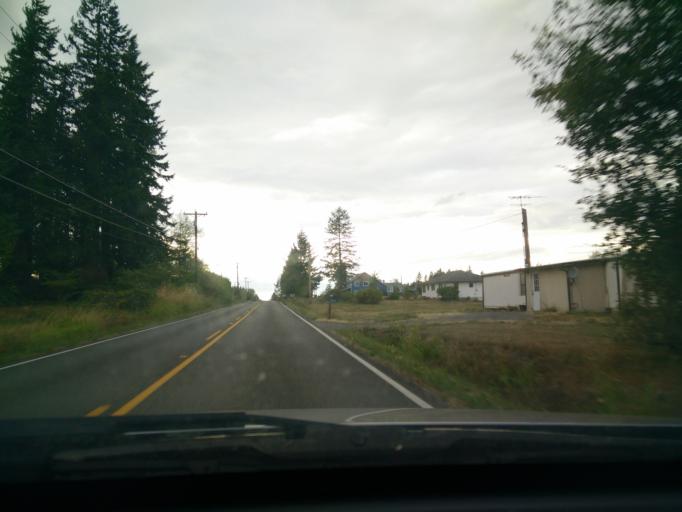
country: US
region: Washington
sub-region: Snohomish County
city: Stanwood
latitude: 48.2684
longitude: -122.2998
